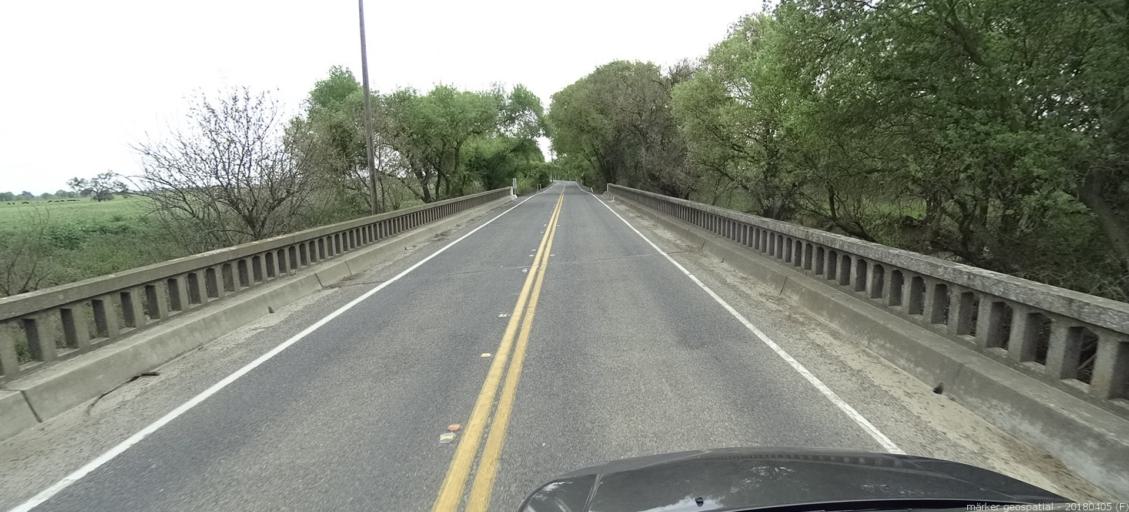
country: US
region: California
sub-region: San Joaquin County
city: Thornton
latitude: 38.2413
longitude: -121.3855
